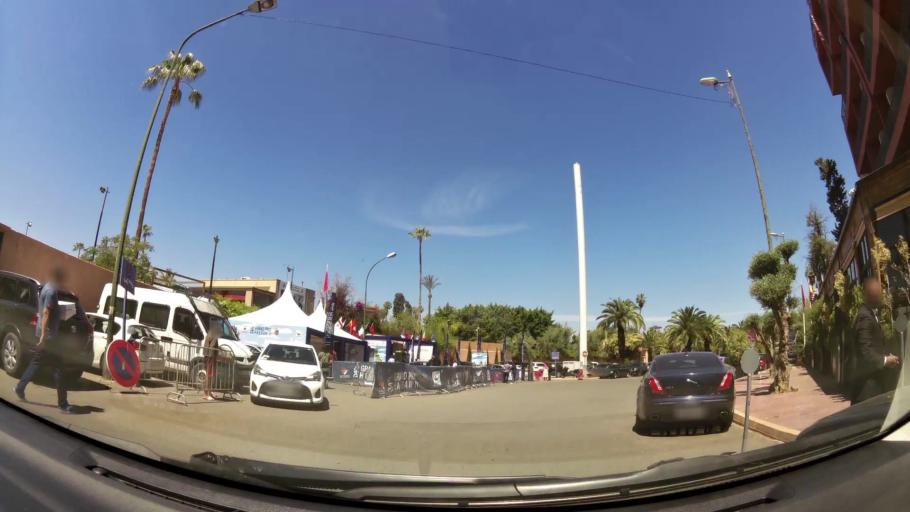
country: MA
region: Marrakech-Tensift-Al Haouz
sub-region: Marrakech
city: Marrakesh
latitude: 31.6292
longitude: -8.0081
